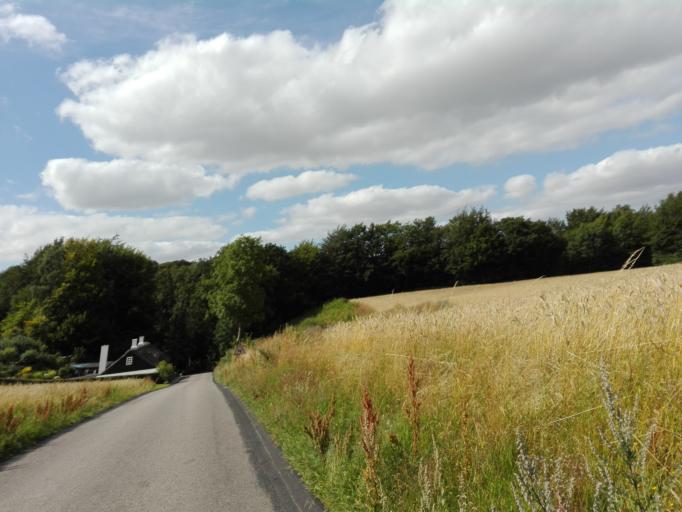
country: DK
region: Central Jutland
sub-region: Skanderborg Kommune
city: Stilling
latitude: 56.1060
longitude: 9.9865
